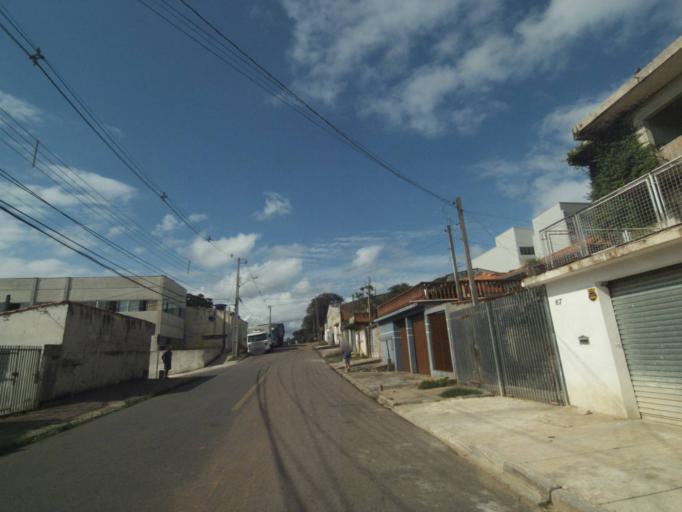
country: BR
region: Parana
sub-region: Curitiba
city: Curitiba
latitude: -25.3810
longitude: -49.2996
